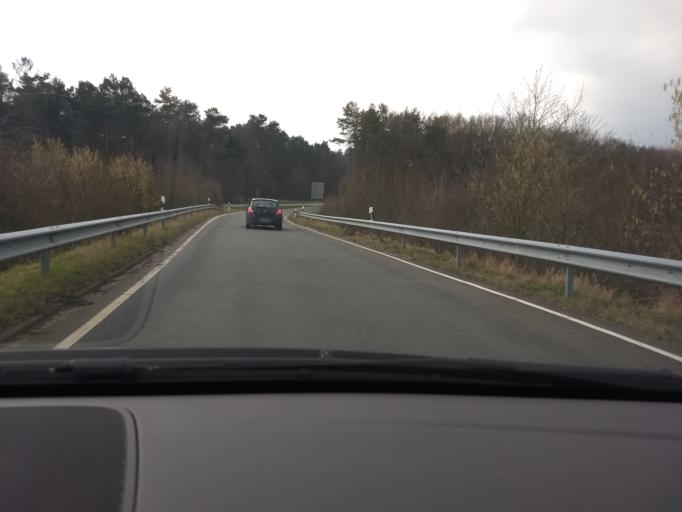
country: DE
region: North Rhine-Westphalia
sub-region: Regierungsbezirk Munster
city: Heiden
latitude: 51.8527
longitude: 6.9207
